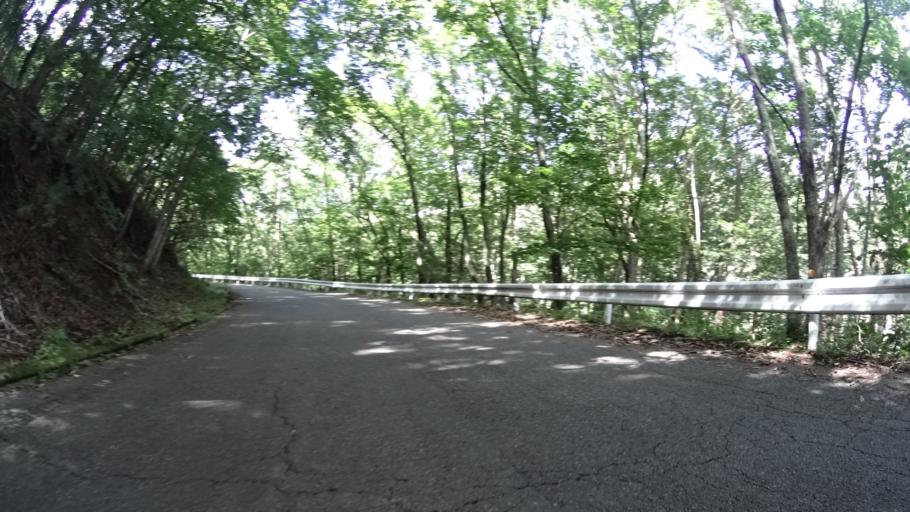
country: JP
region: Yamanashi
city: Nirasaki
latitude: 35.9064
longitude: 138.5424
